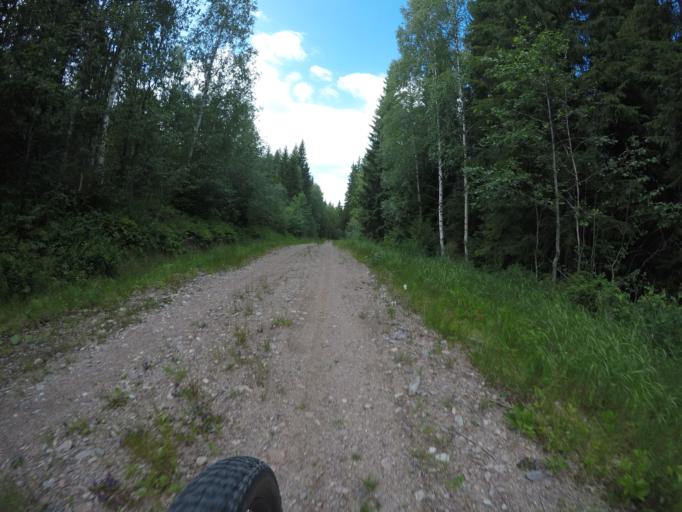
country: SE
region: Dalarna
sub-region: Ludvika Kommun
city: Abborrberget
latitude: 60.0359
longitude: 14.5972
